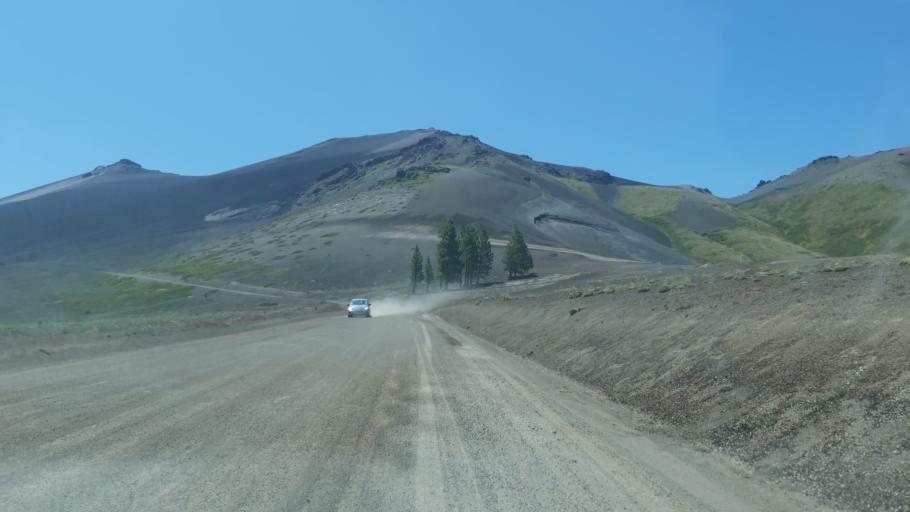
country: CL
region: Araucania
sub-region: Provincia de Cautin
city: Vilcun
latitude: -38.4160
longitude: -71.5429
